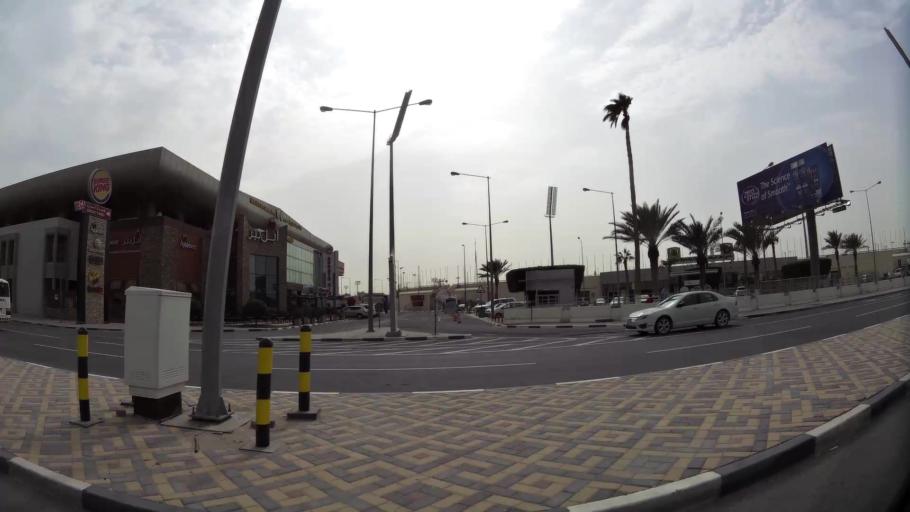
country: QA
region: Baladiyat ad Dawhah
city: Doha
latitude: 25.3173
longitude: 51.5139
